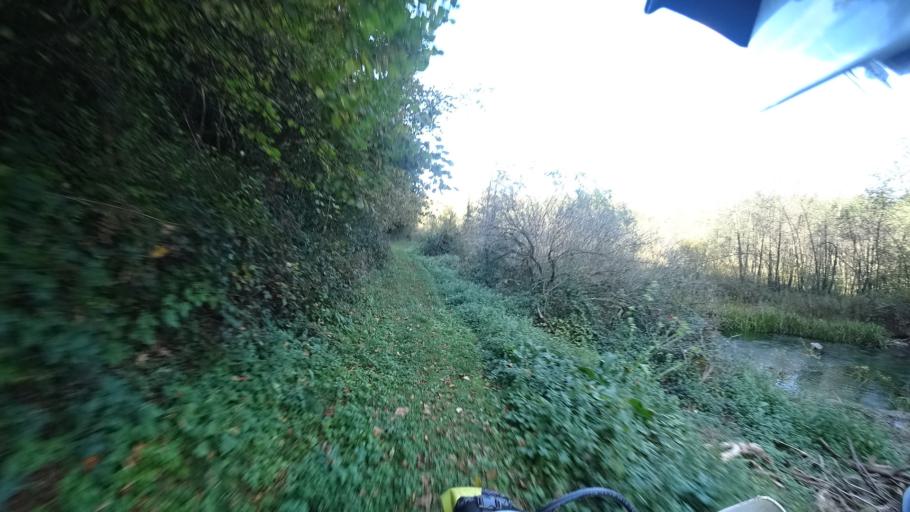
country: HR
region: Karlovacka
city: Plaski
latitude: 45.0749
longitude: 15.3424
